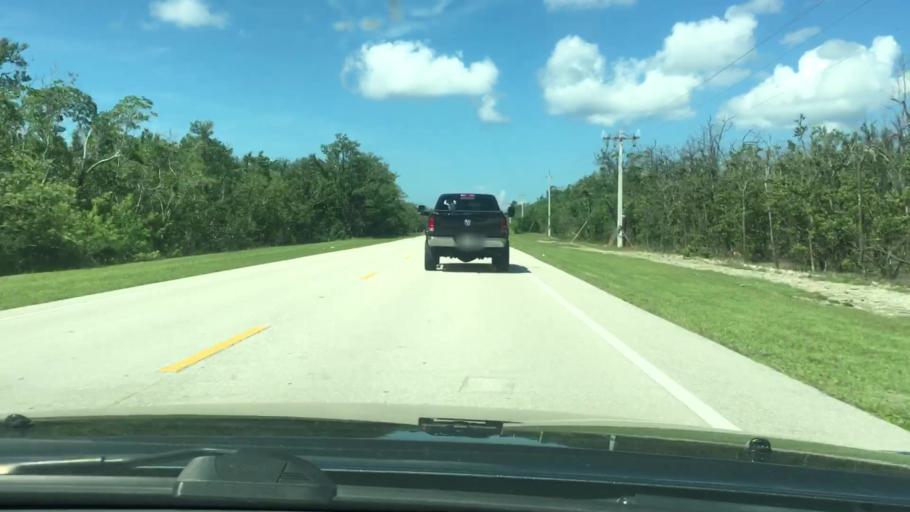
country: US
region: Florida
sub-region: Collier County
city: Marco
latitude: 25.9320
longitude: -81.6645
